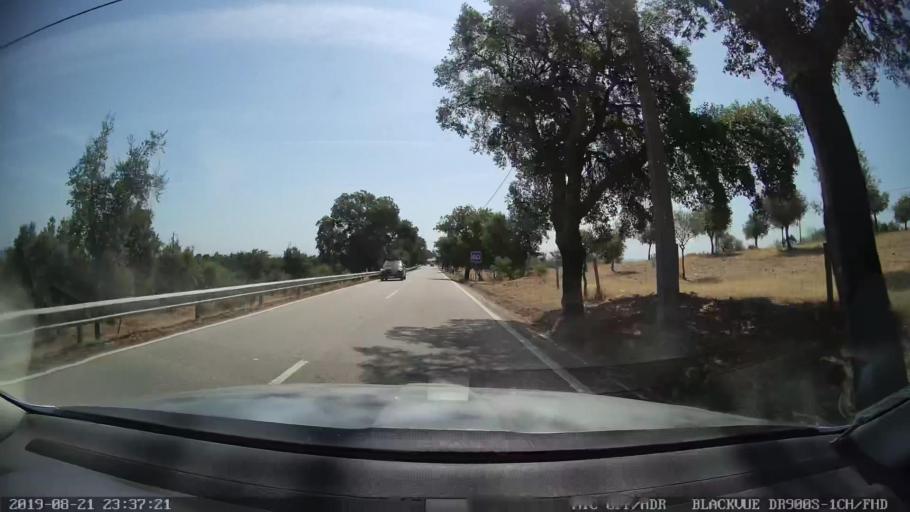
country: PT
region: Guarda
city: Alcains
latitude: 39.8687
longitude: -7.3620
